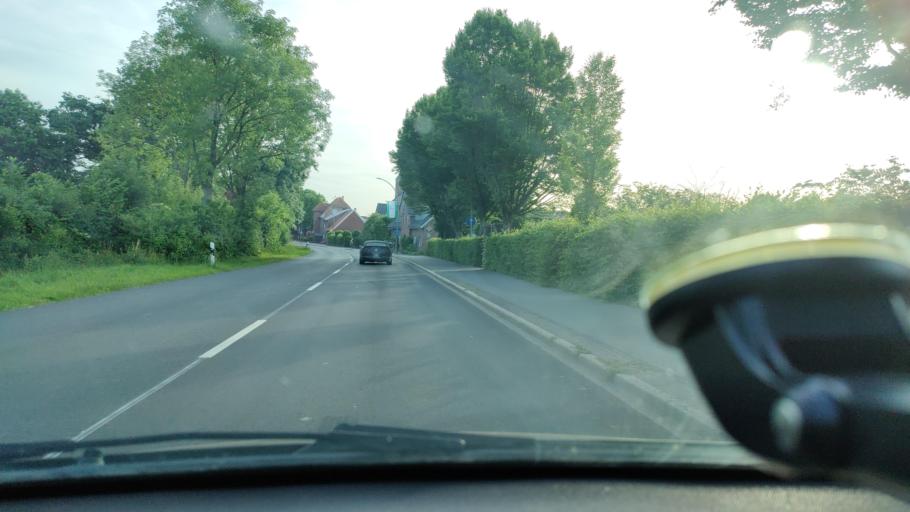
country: DE
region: North Rhine-Westphalia
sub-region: Regierungsbezirk Munster
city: Legden
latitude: 52.0072
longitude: 7.1366
